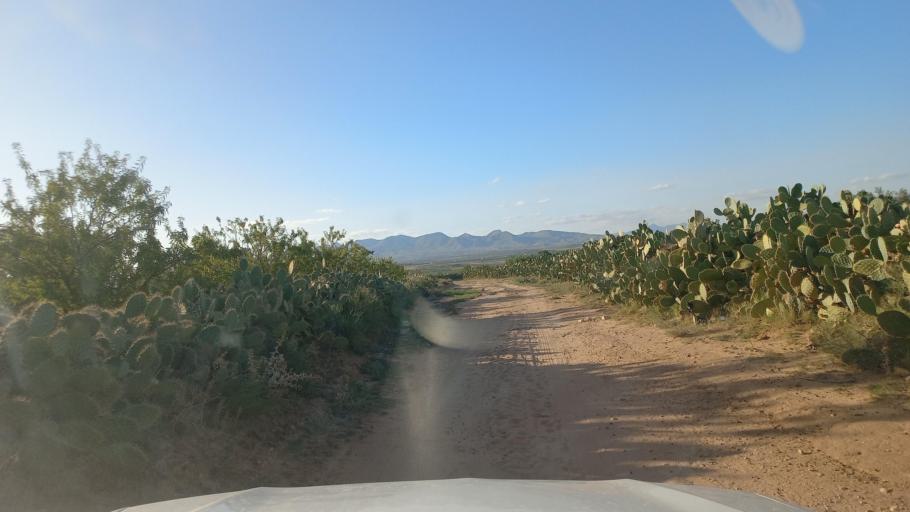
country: TN
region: Al Qasrayn
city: Sbiba
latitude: 35.3854
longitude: 9.1560
